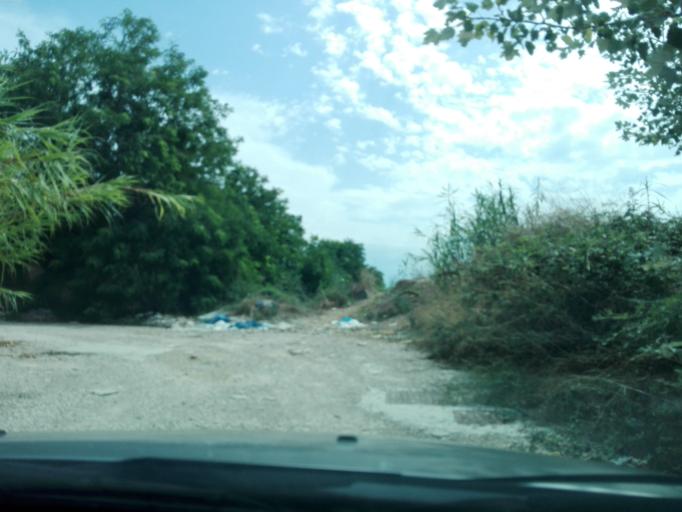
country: IT
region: Abruzzo
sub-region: Provincia di Pescara
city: Cappelle sul Tavo
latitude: 42.4888
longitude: 14.1114
